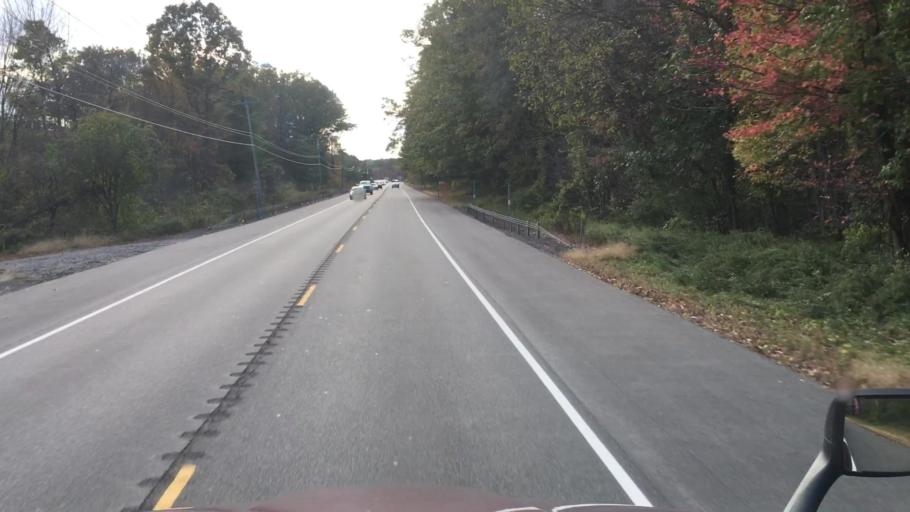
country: US
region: New York
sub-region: Saratoga County
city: North Ballston Spa
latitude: 43.0272
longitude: -73.8338
